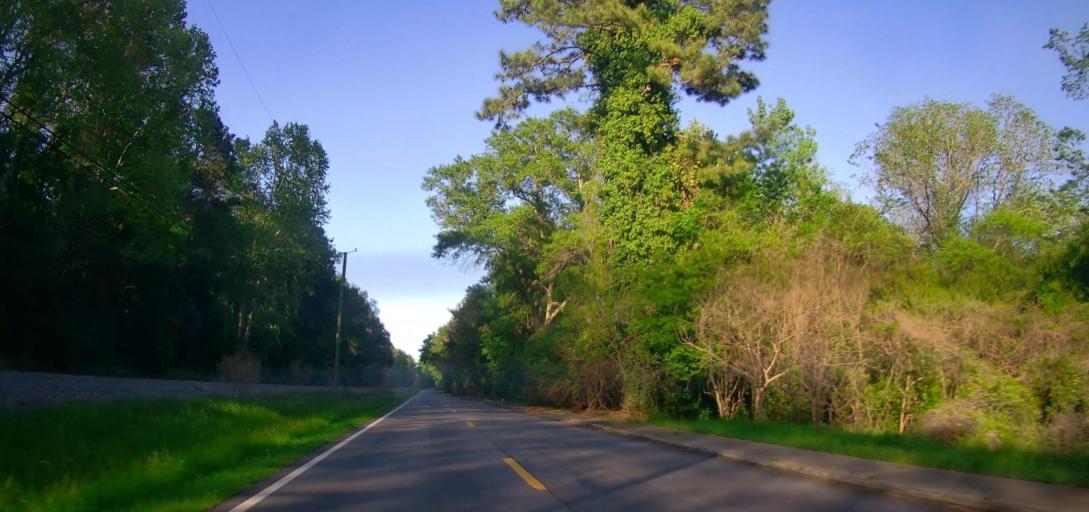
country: US
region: Georgia
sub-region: Macon County
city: Montezuma
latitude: 32.3051
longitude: -84.0224
